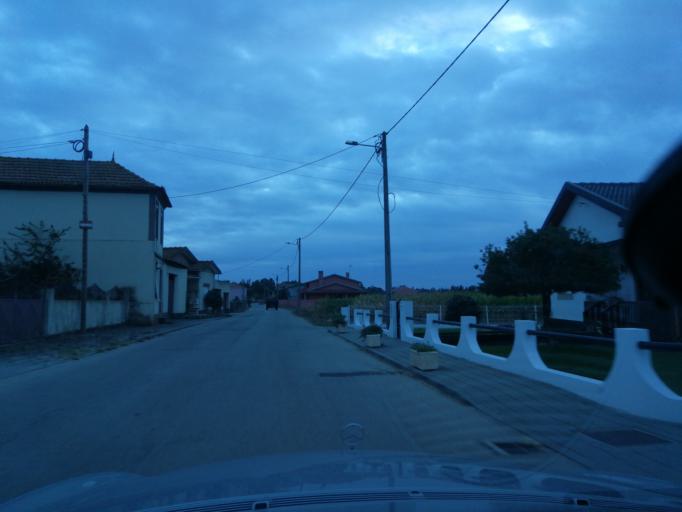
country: PT
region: Aveiro
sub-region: Estarreja
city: Estarreja
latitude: 40.7673
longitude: -8.5956
